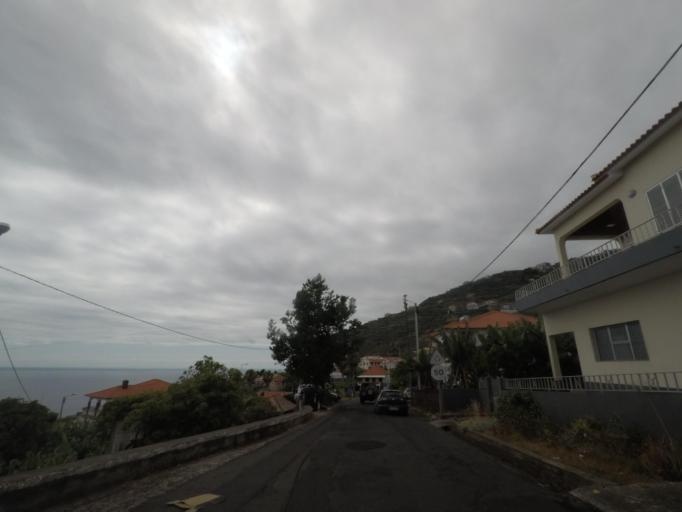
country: PT
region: Madeira
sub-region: Calheta
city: Arco da Calheta
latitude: 32.7124
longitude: -17.1516
